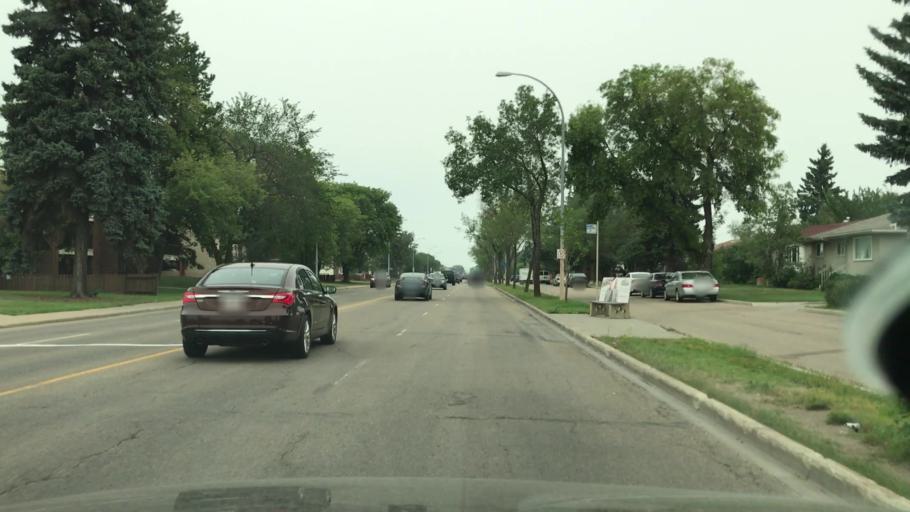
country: CA
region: Alberta
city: Edmonton
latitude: 53.5347
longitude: -113.5779
